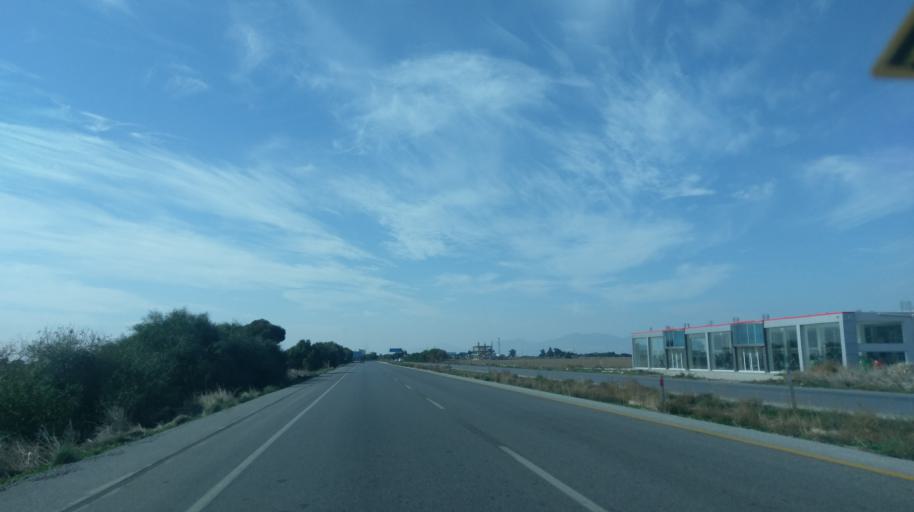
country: CY
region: Ammochostos
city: Lefkonoiko
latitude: 35.1718
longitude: 33.7732
